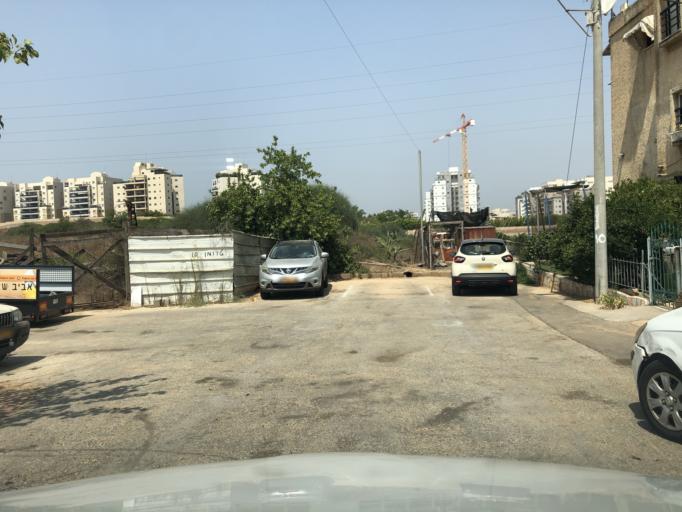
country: IL
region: Central District
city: Ganne Tiqwa
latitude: 32.0695
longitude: 34.8745
